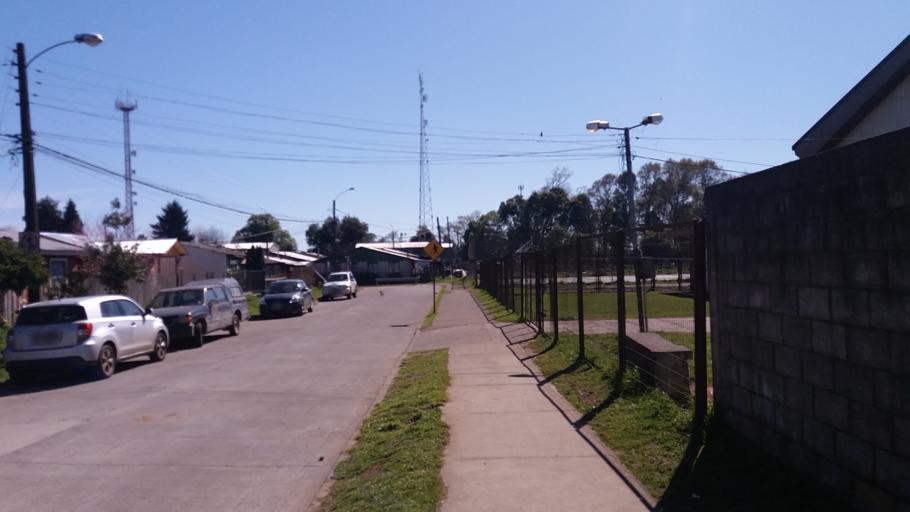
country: CL
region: Araucania
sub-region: Provincia de Cautin
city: Carahue
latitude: -39.1768
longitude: -73.1669
